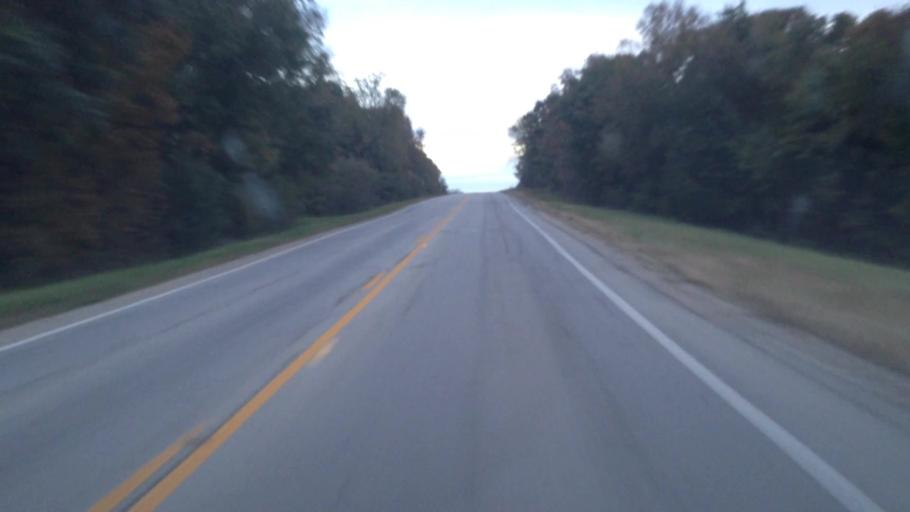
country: US
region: Kansas
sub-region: Anderson County
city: Garnett
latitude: 38.2483
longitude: -95.2484
